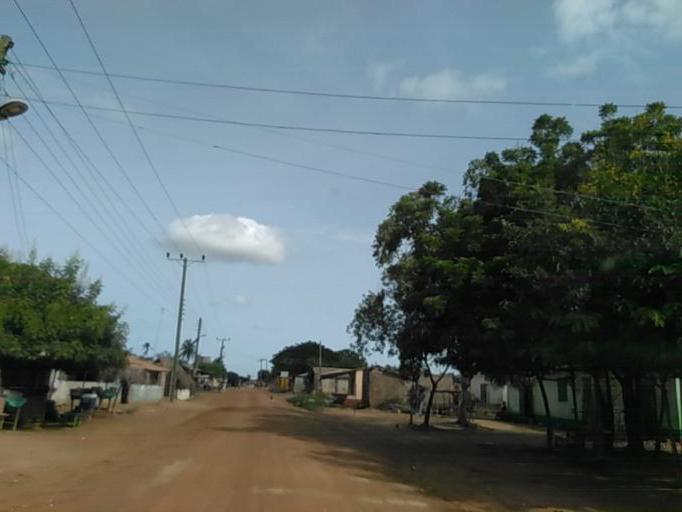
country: GH
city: Akropong
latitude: 6.0313
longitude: 0.3748
